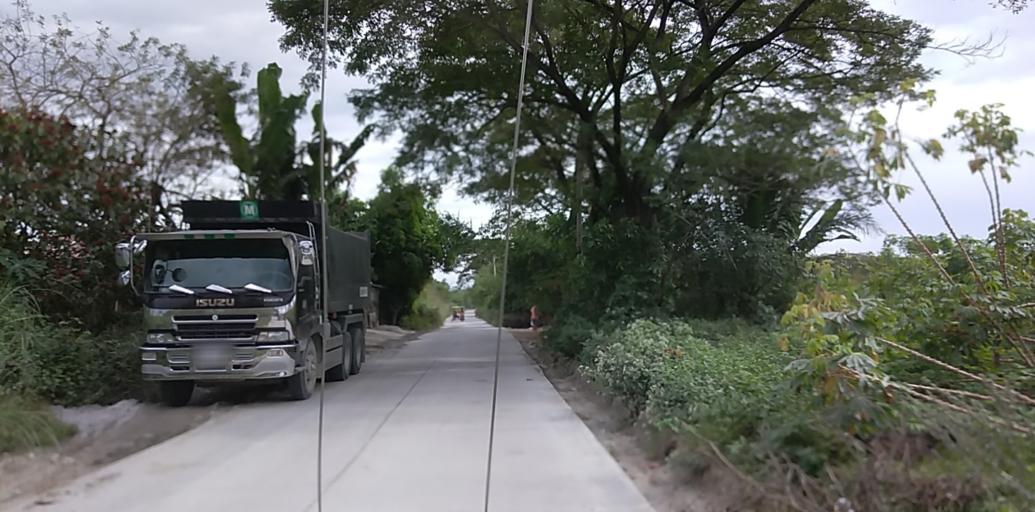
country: PH
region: Central Luzon
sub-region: Province of Pampanga
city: Pulung Santol
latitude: 15.0587
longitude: 120.5555
